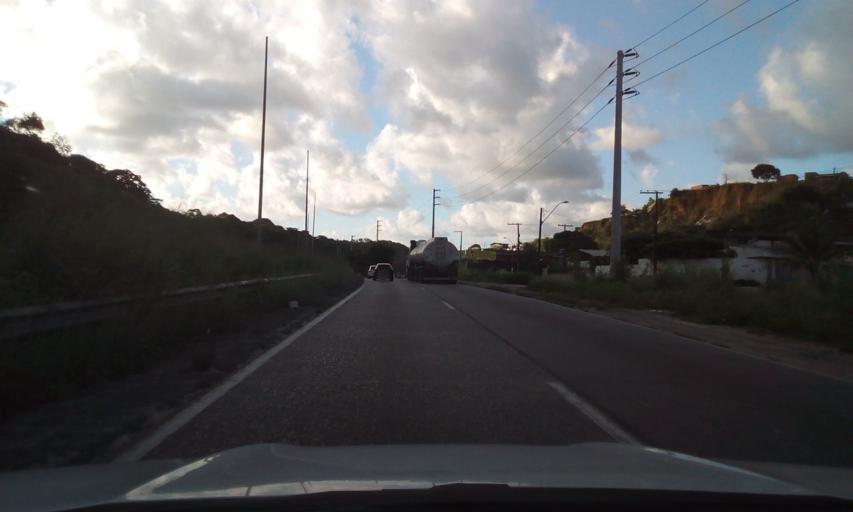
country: BR
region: Pernambuco
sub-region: Recife
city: Recife
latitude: -8.0009
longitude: -34.9386
